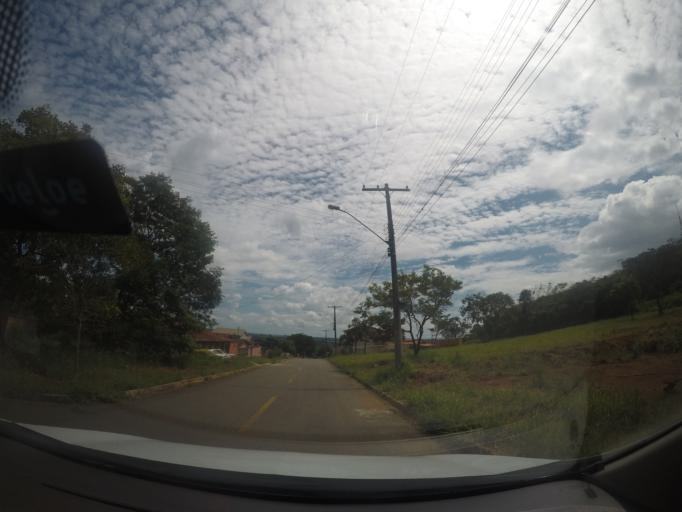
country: BR
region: Goias
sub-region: Goiania
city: Goiania
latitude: -16.6641
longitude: -49.3473
